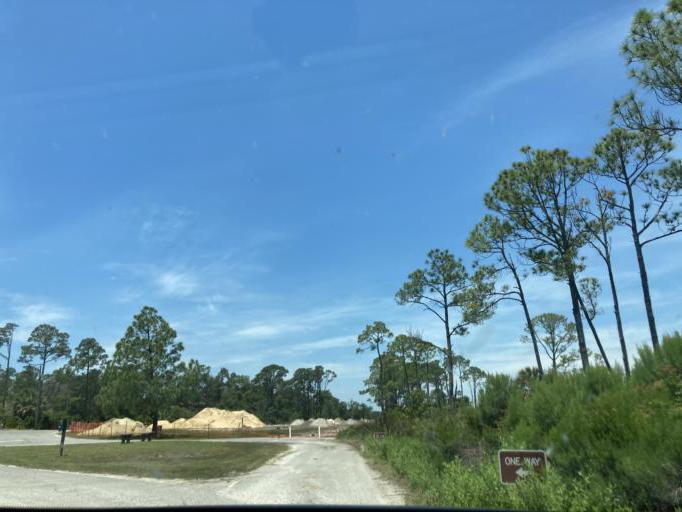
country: US
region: Florida
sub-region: Bay County
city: Lower Grand Lagoon
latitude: 30.1372
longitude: -85.7363
